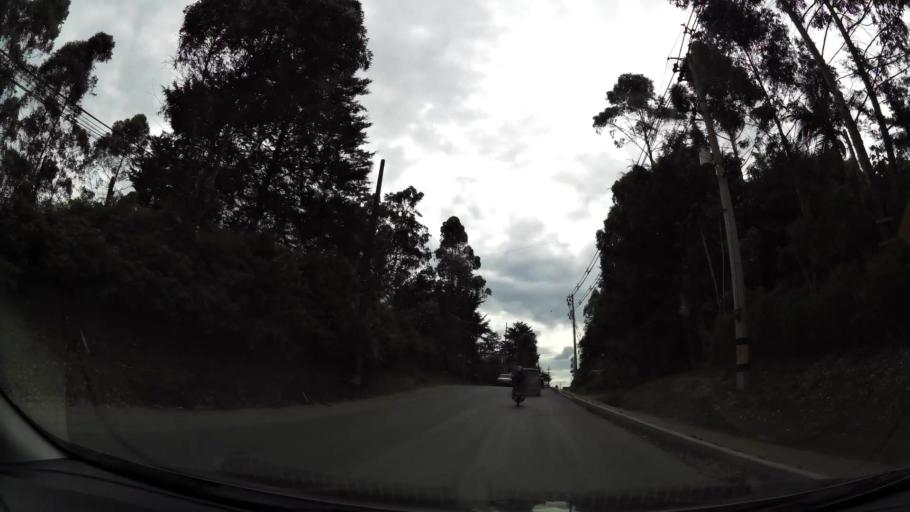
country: CO
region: Antioquia
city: Rionegro
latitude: 6.1525
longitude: -75.4014
